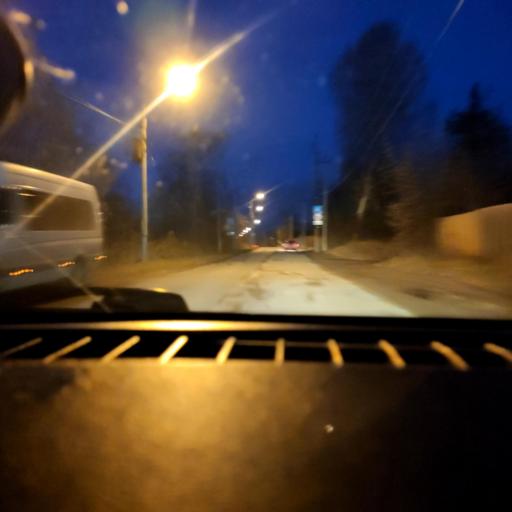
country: RU
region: Perm
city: Perm
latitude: 58.0273
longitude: 56.1944
